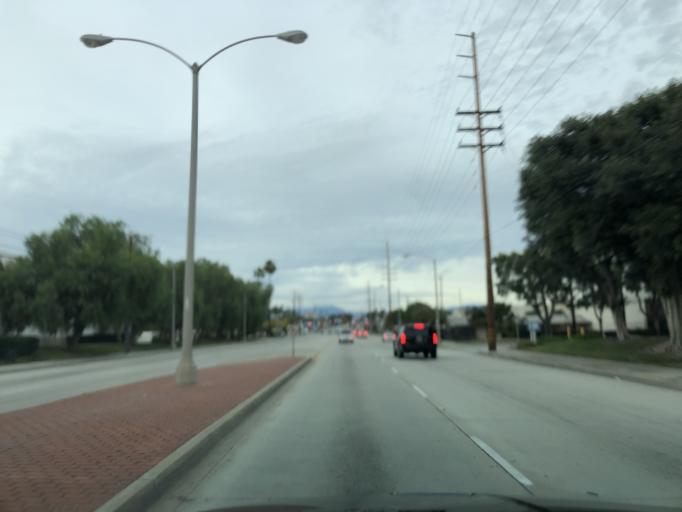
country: US
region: California
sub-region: Los Angeles County
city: La Mirada
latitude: 33.9146
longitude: -118.0467
